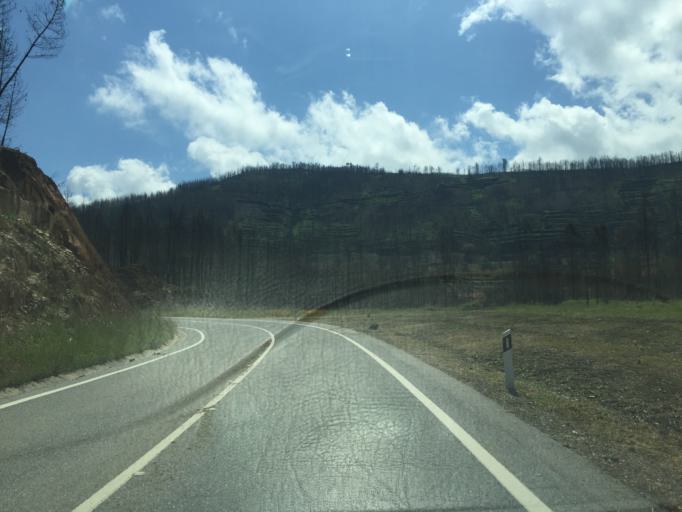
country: PT
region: Coimbra
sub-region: Pampilhosa da Serra
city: Pampilhosa da Serra
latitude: 39.9796
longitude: -7.9598
